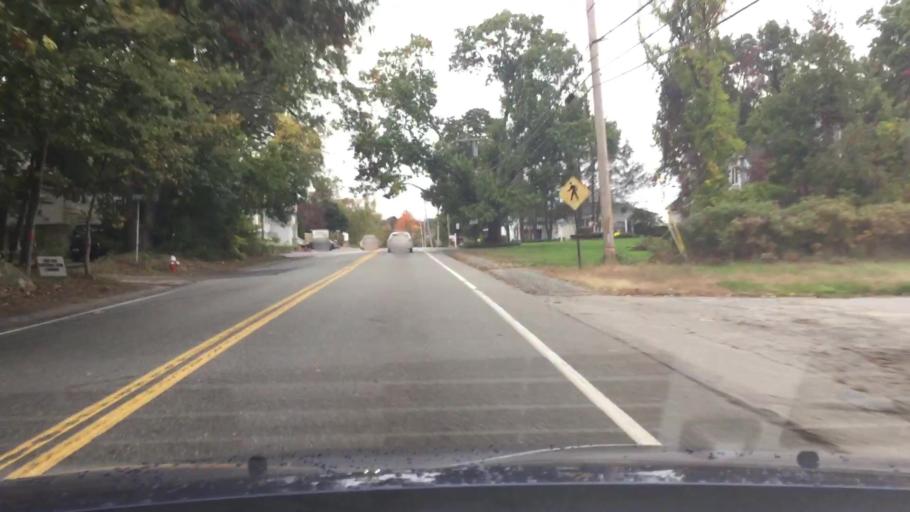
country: US
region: Massachusetts
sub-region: Middlesex County
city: Tyngsboro
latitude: 42.6801
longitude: -71.3660
